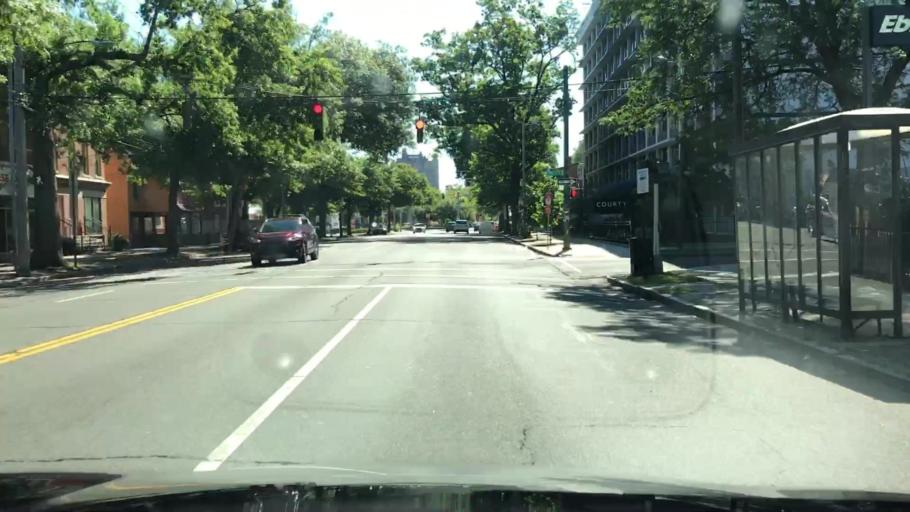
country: US
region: Connecticut
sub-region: New Haven County
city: New Haven
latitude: 41.3136
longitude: -72.9345
